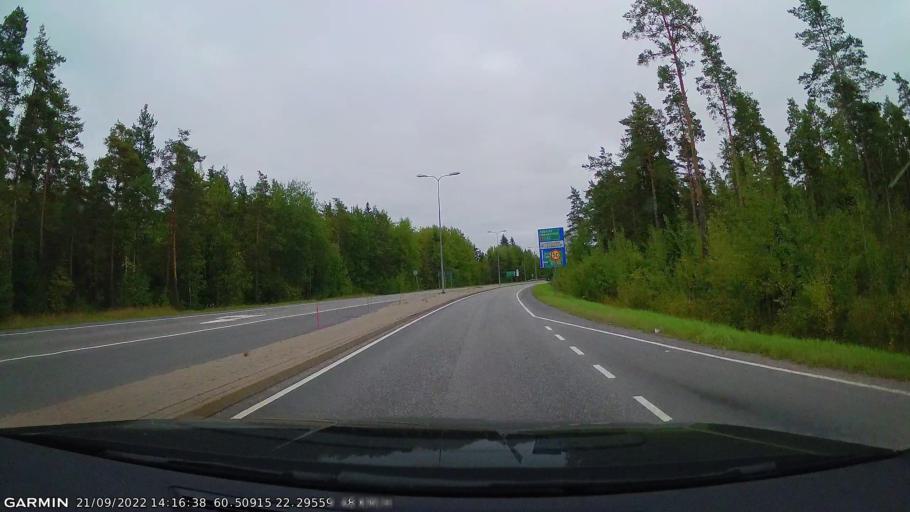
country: FI
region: Varsinais-Suomi
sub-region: Turku
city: Turku
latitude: 60.5092
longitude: 22.2956
